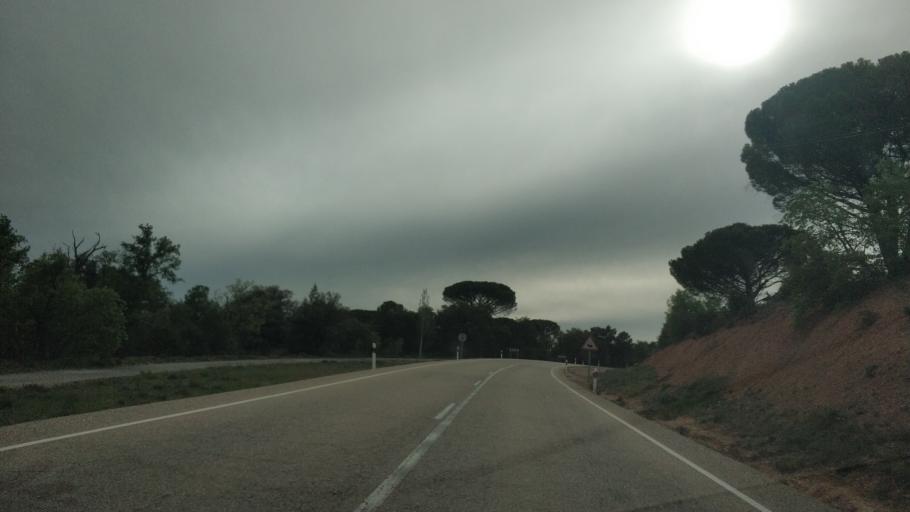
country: ES
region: Castille and Leon
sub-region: Provincia de Soria
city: Bayubas de Abajo
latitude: 41.5046
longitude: -2.8953
